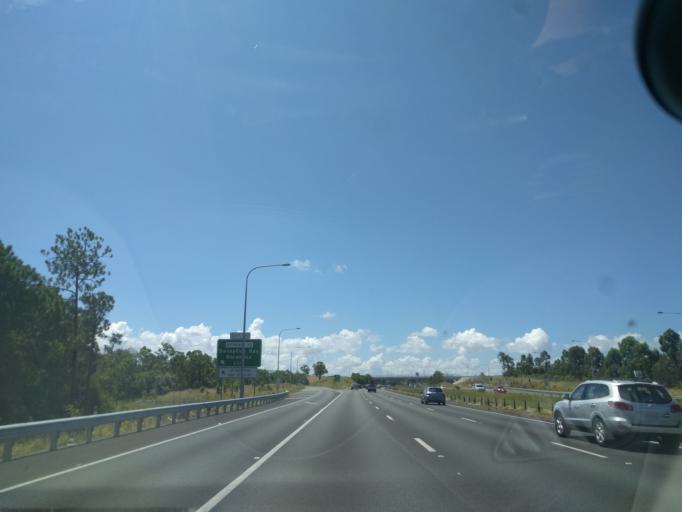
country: AU
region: Queensland
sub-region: Moreton Bay
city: Narangba
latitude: -27.2159
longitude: 152.9945
